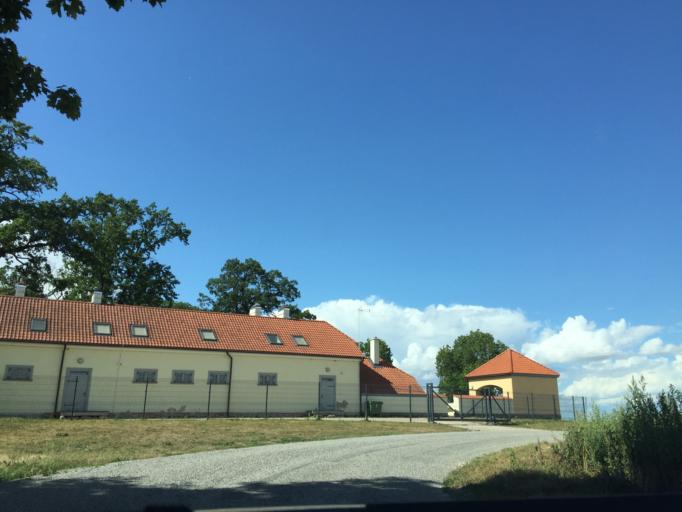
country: LT
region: Siauliu apskritis
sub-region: Joniskis
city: Joniskis
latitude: 56.3441
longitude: 23.5489
